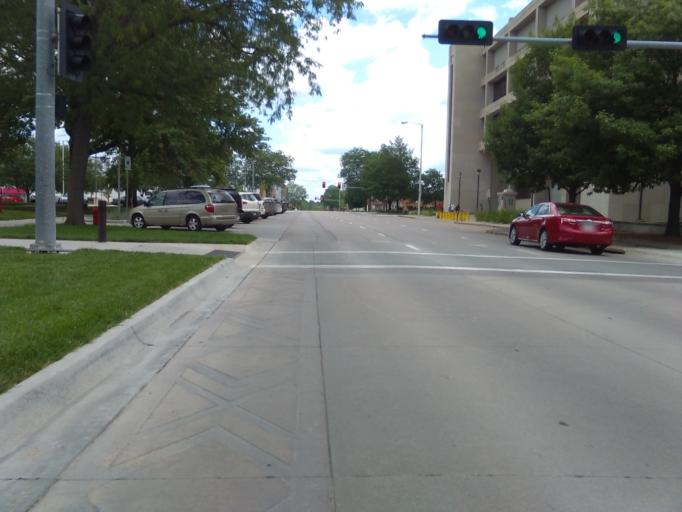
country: US
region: Nebraska
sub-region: Lancaster County
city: Lincoln
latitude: 40.8147
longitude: -96.6997
